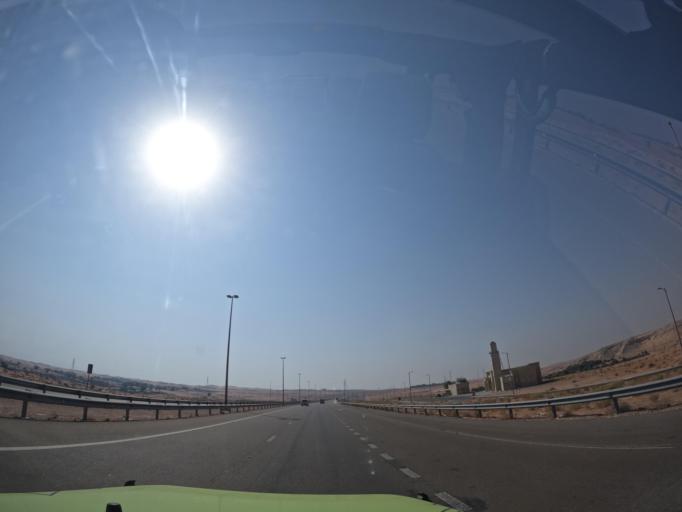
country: OM
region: Al Buraimi
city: Al Buraymi
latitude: 24.3927
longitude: 55.7221
